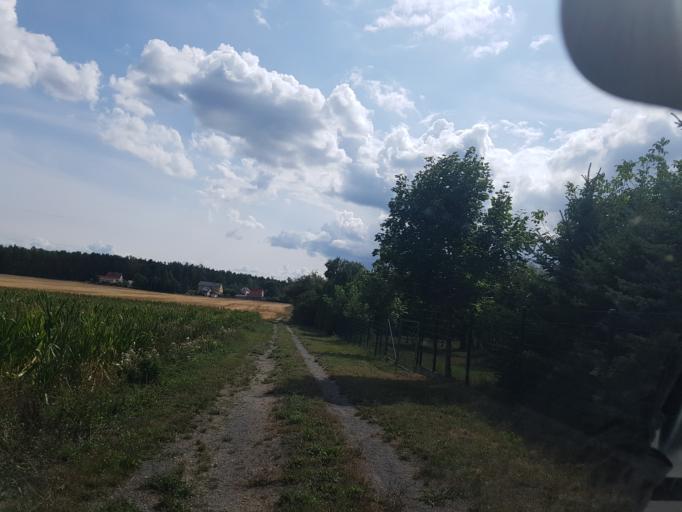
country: DE
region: Brandenburg
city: Schonborn
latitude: 51.6700
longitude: 13.4746
